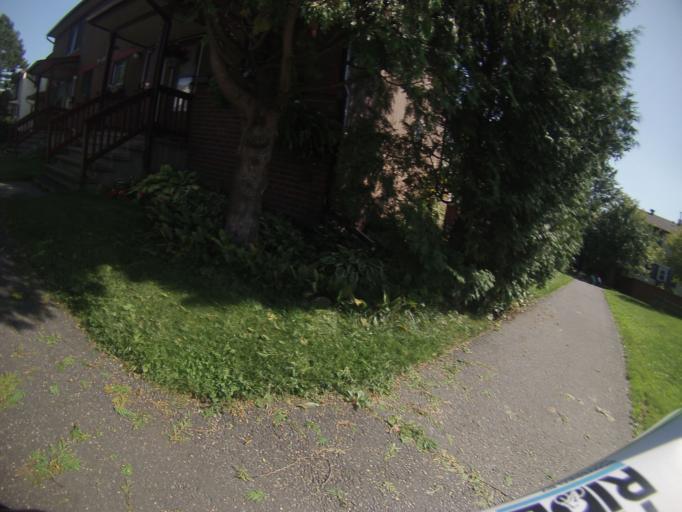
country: CA
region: Ontario
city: Ottawa
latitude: 45.3646
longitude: -75.6431
